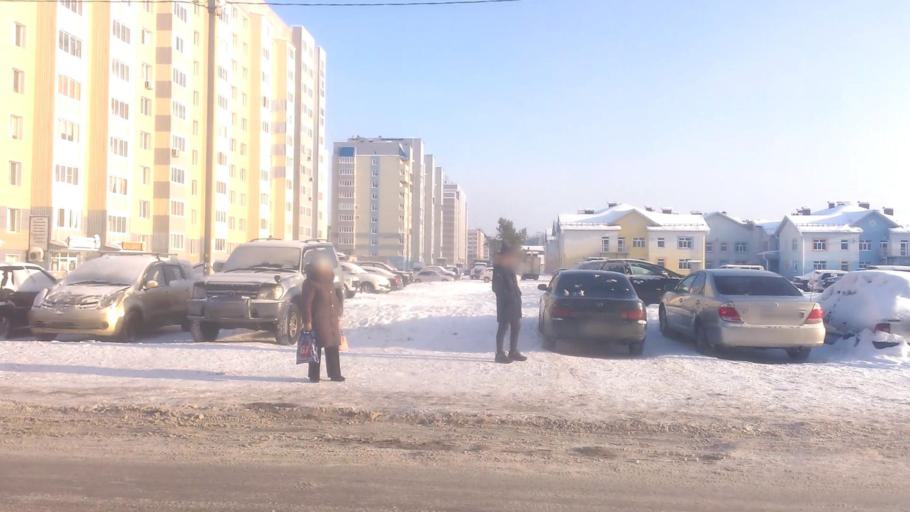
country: RU
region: Altai Krai
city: Novosilikatnyy
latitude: 53.3439
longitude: 83.6555
